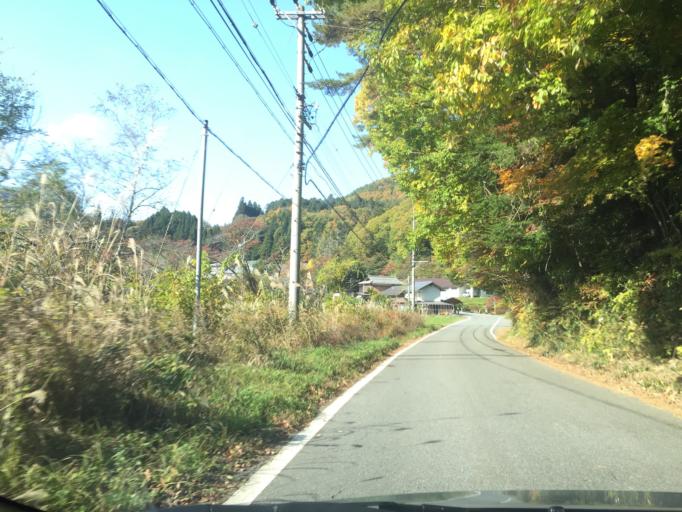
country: JP
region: Nagano
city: Iida
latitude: 35.3732
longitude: 137.6939
